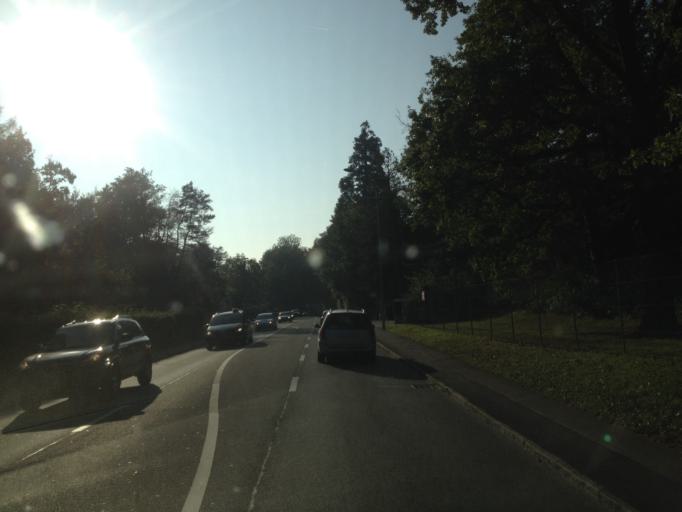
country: CH
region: Geneva
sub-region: Geneva
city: Le Grand-Saconnex
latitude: 46.2292
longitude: 6.1268
